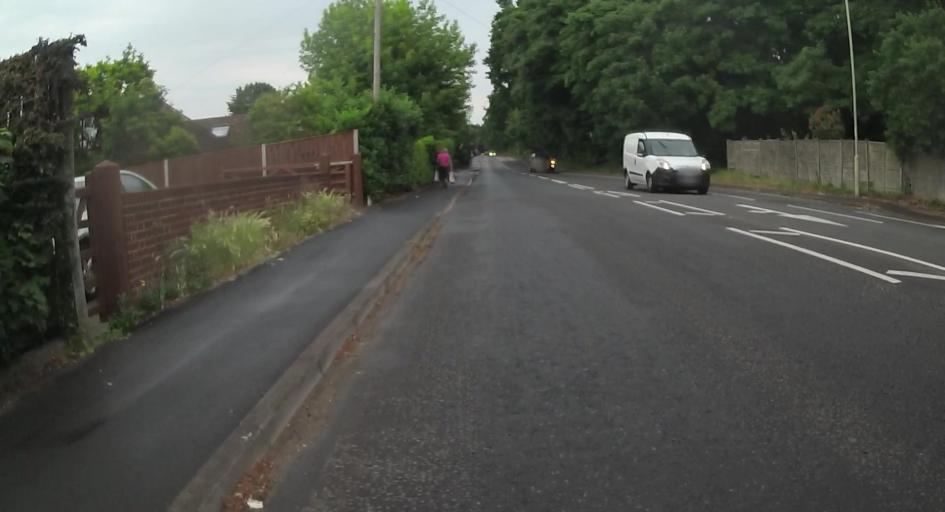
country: GB
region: England
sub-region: Hampshire
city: Fleet
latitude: 51.2636
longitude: -0.8270
